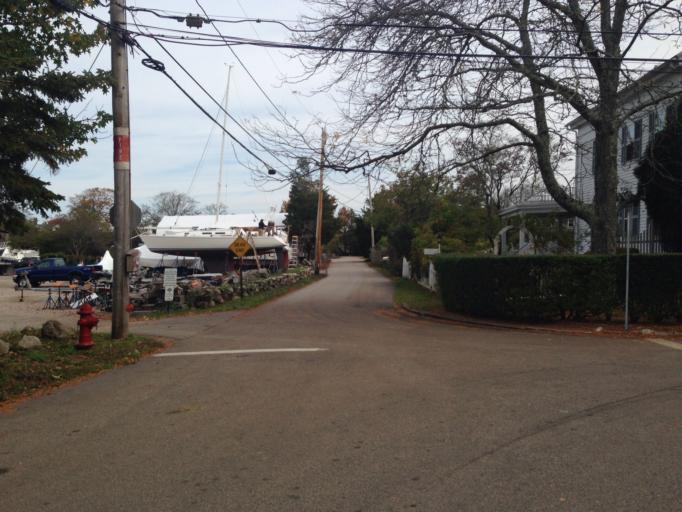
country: US
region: Connecticut
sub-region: New London County
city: Pawcatuck
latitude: 41.3341
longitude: -71.8358
